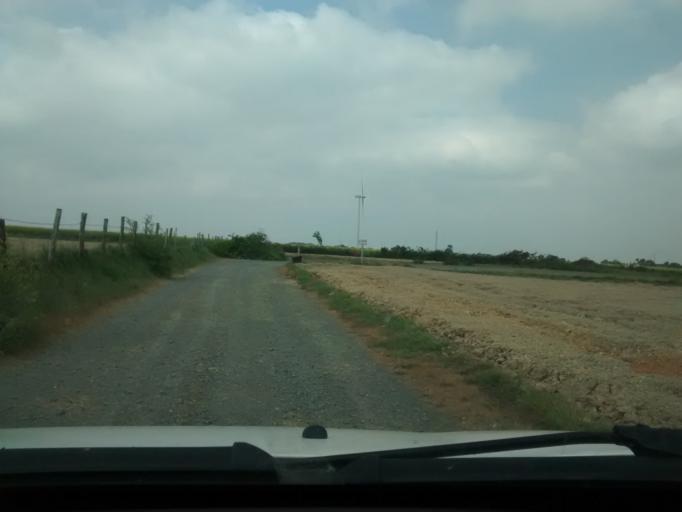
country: FR
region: Brittany
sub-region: Departement d'Ille-et-Vilaine
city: Grand-Fougeray
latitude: 47.7752
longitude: -1.7496
